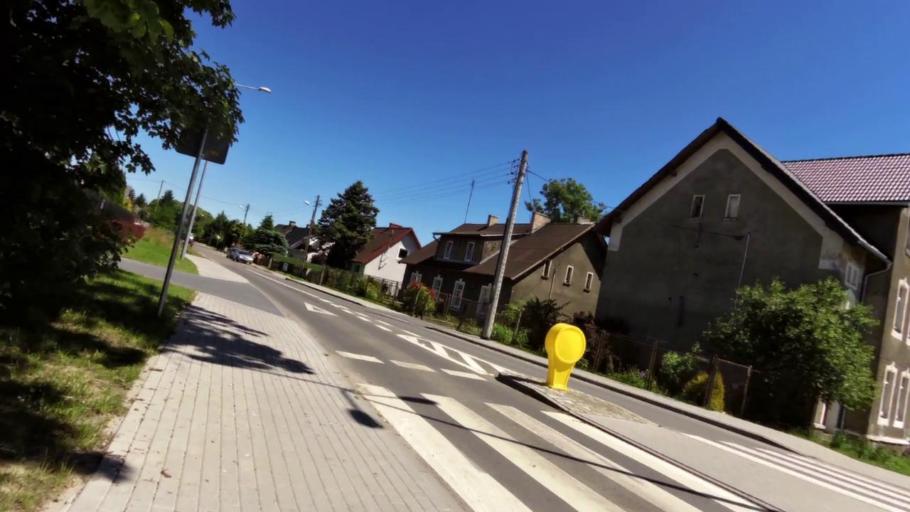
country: PL
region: West Pomeranian Voivodeship
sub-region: Powiat kolobrzeski
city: Goscino
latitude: 54.0537
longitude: 15.6451
